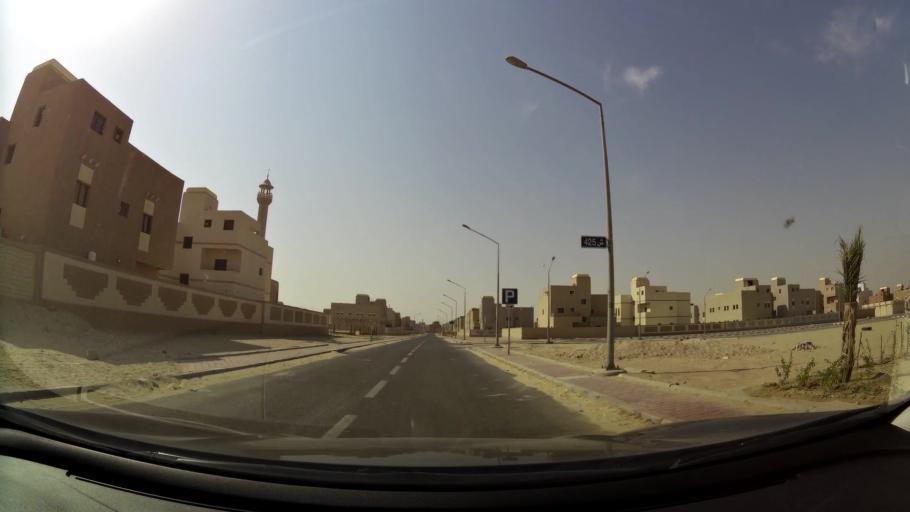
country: KW
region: Al Ahmadi
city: Al Wafrah
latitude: 28.7999
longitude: 48.0762
